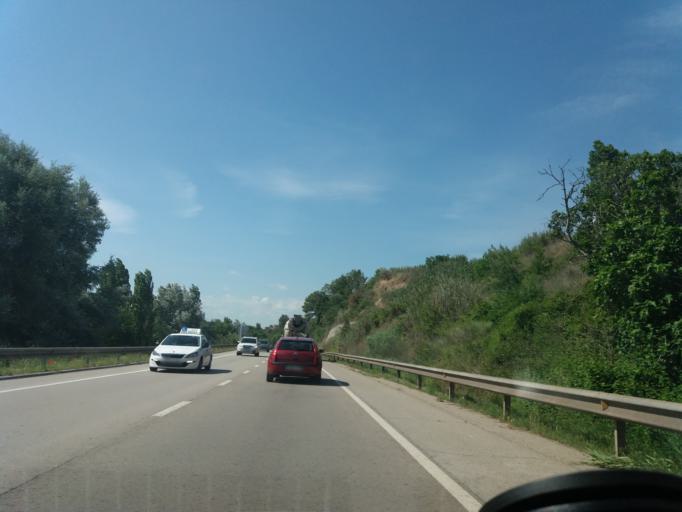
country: ES
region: Catalonia
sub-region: Provincia de Barcelona
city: Manresa
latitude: 41.7304
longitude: 1.8141
